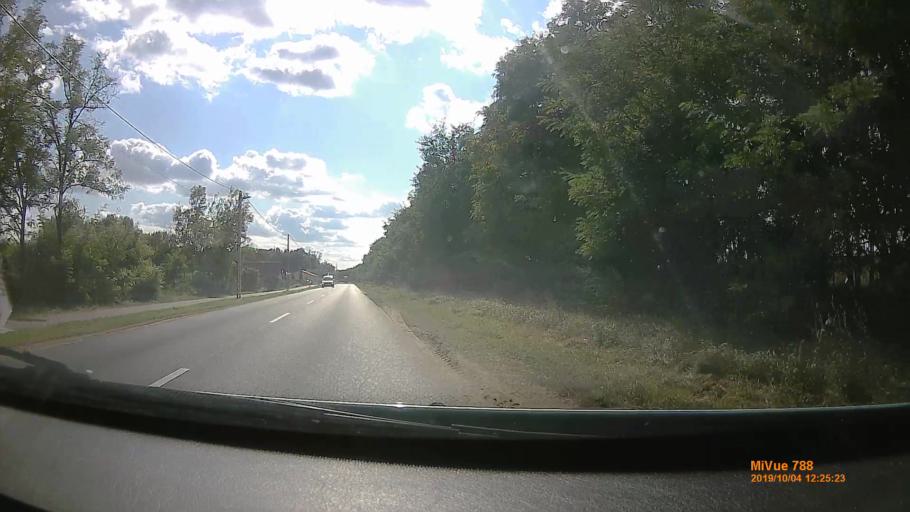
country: HU
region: Szabolcs-Szatmar-Bereg
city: Nyiregyhaza
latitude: 47.9868
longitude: 21.7043
